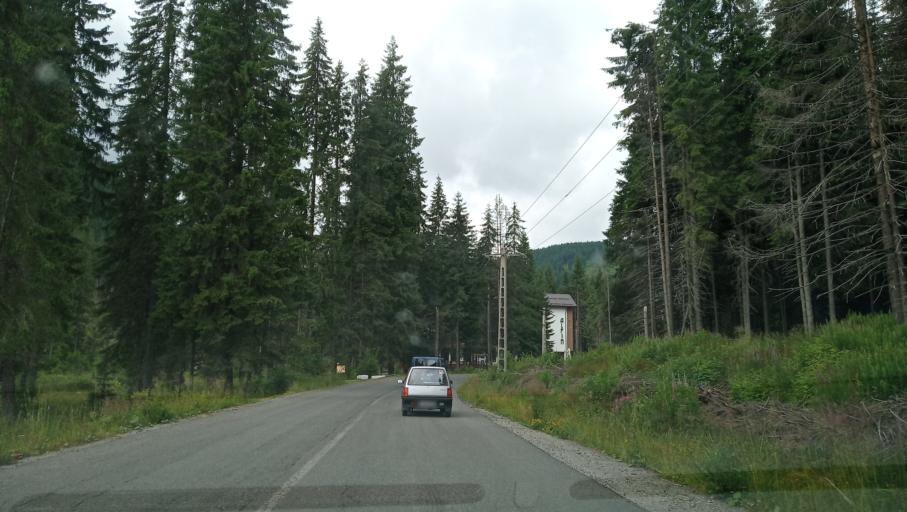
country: RO
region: Hunedoara
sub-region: Oras Petrila
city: Petrila
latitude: 45.4345
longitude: 23.6378
